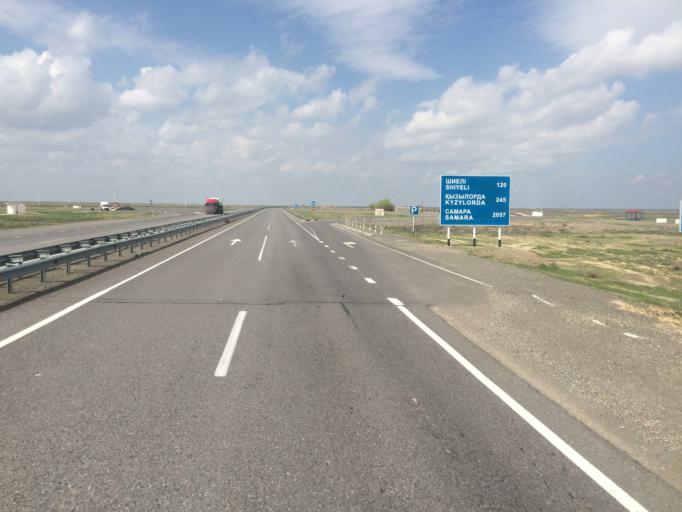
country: KZ
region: Ongtustik Qazaqstan
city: Turkestan
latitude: 43.5309
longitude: 67.7829
